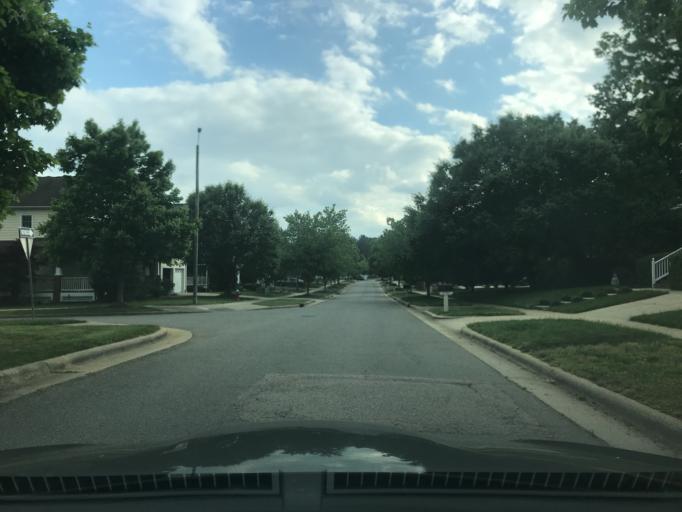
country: US
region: North Carolina
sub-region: Wake County
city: Wake Forest
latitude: 35.9192
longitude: -78.5644
